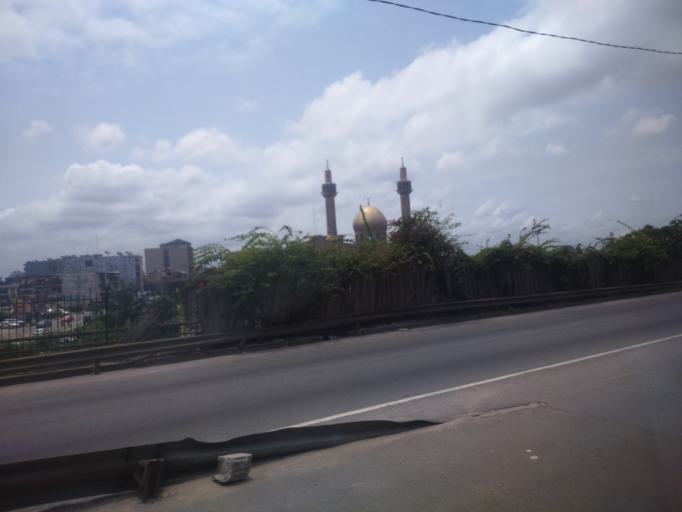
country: CI
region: Lagunes
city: Abidjan
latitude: 5.3060
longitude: -3.9967
